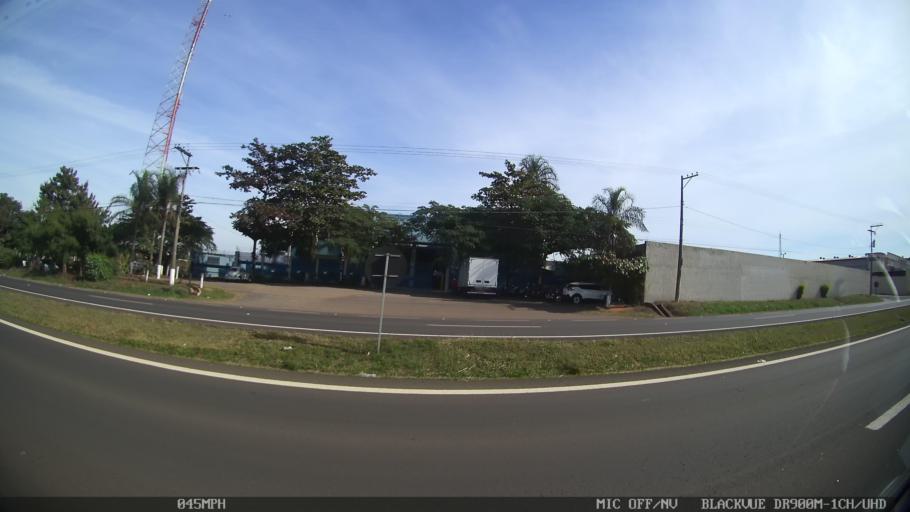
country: BR
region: Sao Paulo
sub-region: Piracicaba
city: Piracicaba
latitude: -22.7672
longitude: -47.6463
